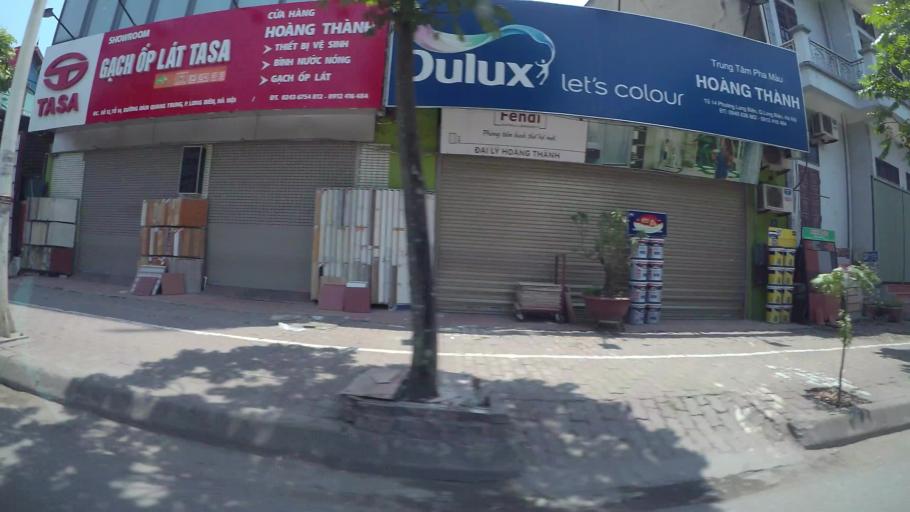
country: VN
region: Ha Noi
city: Trau Quy
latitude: 21.0224
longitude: 105.8938
